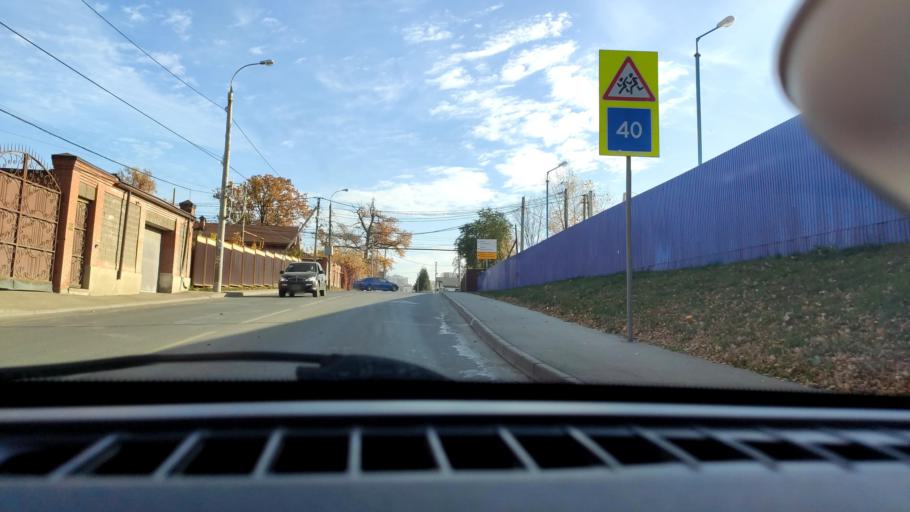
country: RU
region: Samara
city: Samara
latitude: 53.2714
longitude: 50.1949
